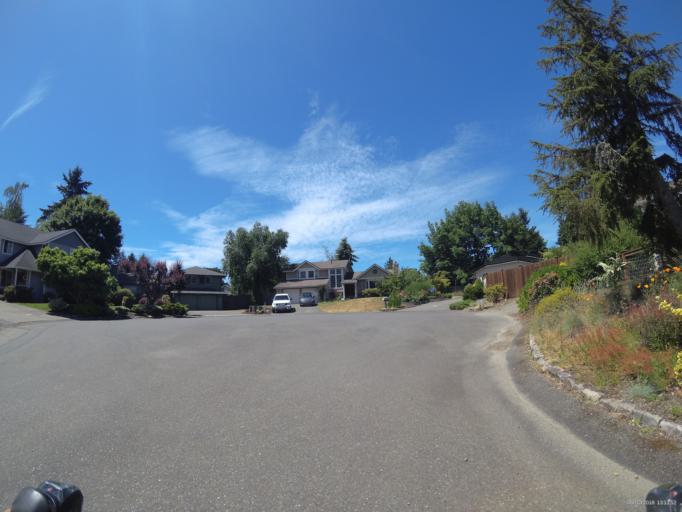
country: US
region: Washington
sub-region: Pierce County
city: University Place
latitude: 47.2049
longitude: -122.5659
